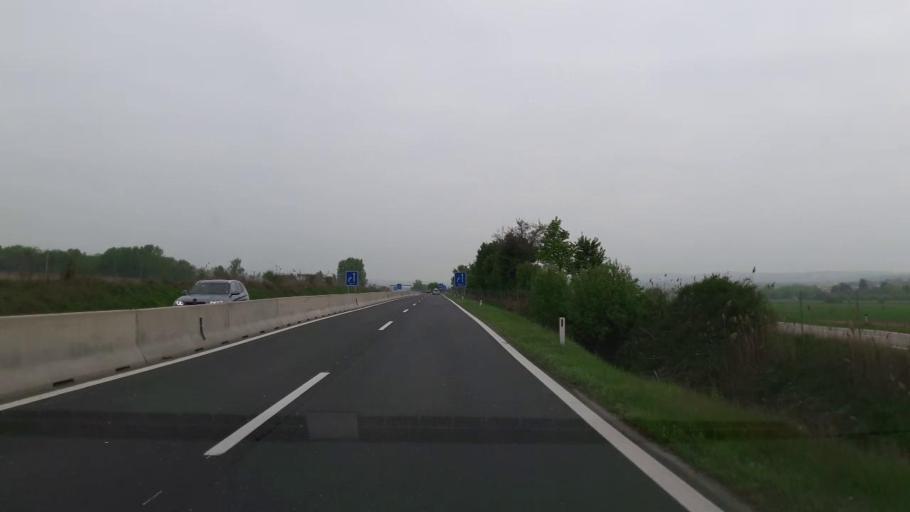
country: AT
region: Lower Austria
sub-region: Politischer Bezirk Korneuburg
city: Sierndorf
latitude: 48.4473
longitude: 16.1628
